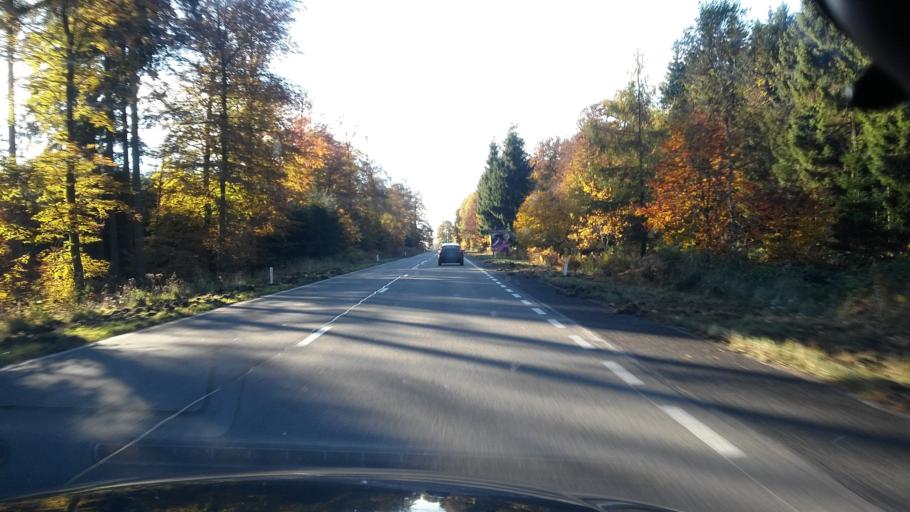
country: BE
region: Wallonia
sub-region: Province du Luxembourg
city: Herbeumont
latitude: 49.7537
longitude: 5.1708
